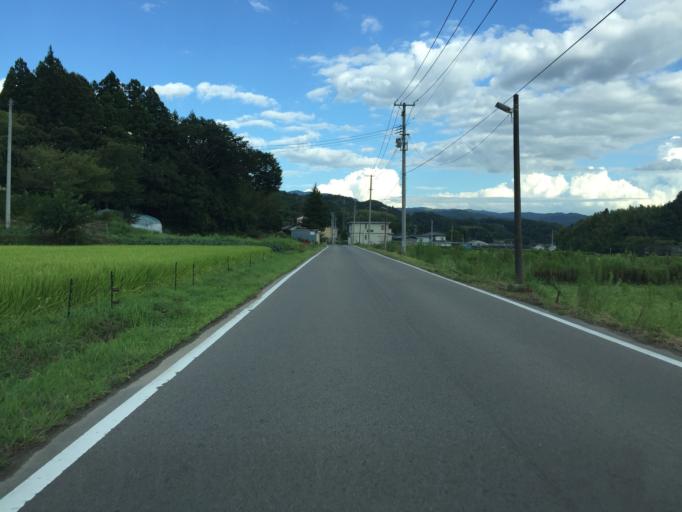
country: JP
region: Fukushima
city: Fukushima-shi
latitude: 37.6793
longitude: 140.5766
